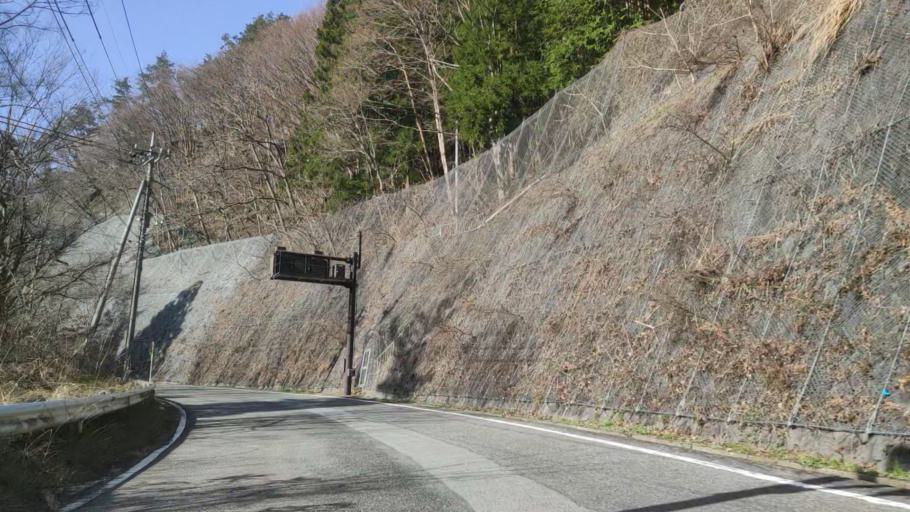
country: JP
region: Yamanashi
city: Fujikawaguchiko
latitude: 35.5317
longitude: 138.6213
